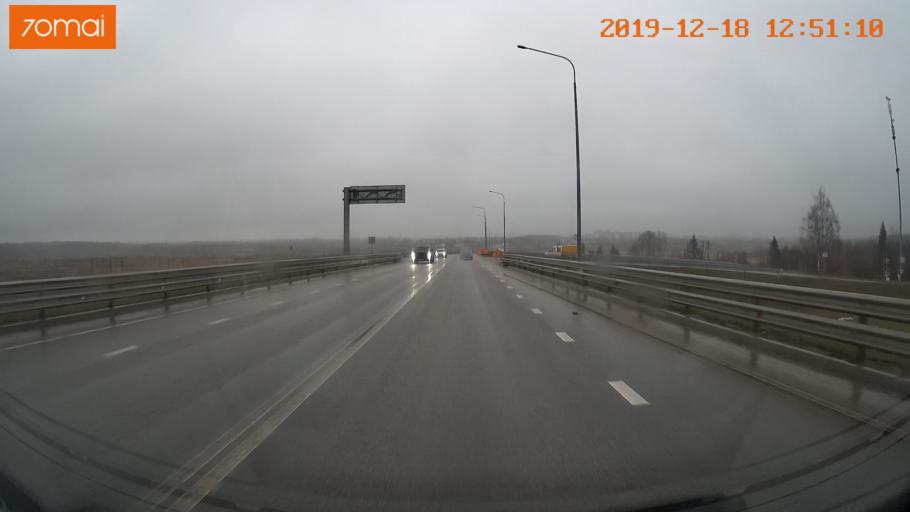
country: RU
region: Moskovskaya
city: Klin
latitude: 56.3007
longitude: 36.6824
